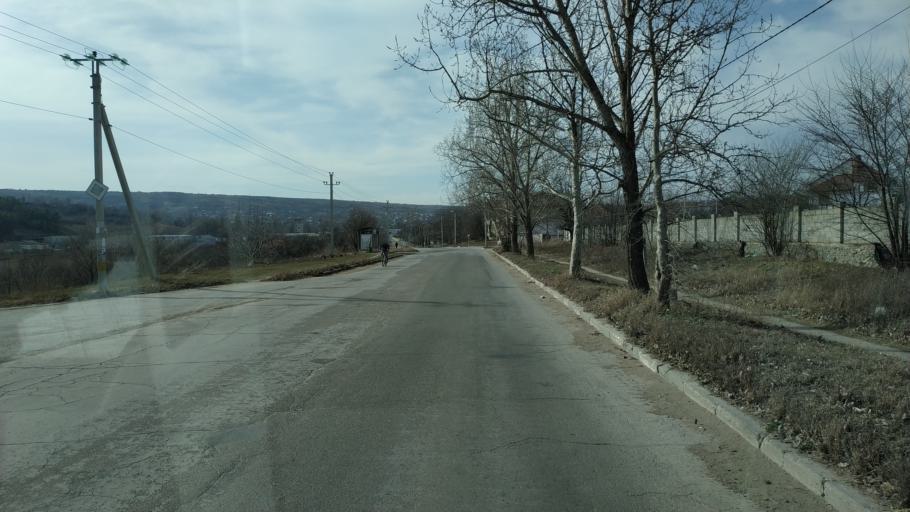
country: MD
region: Chisinau
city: Vatra
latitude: 47.0721
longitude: 28.6978
